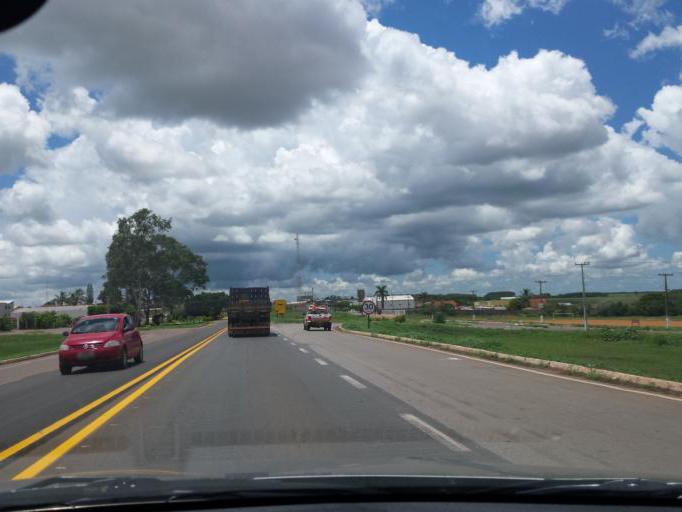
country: BR
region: Goias
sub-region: Cristalina
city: Cristalina
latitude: -16.7653
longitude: -47.6153
